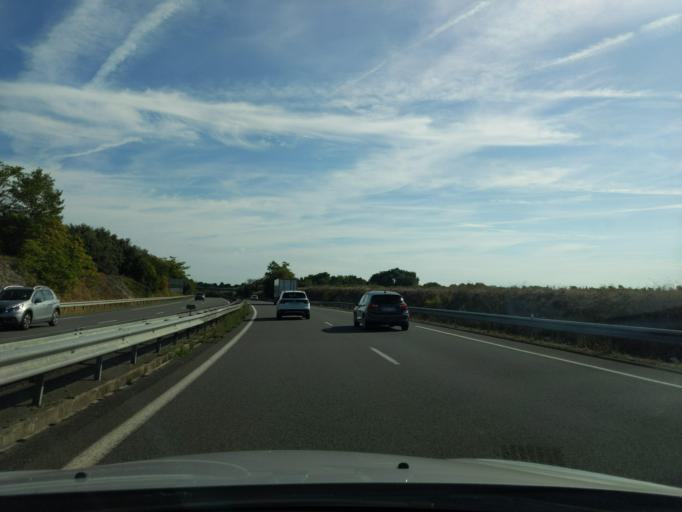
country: FR
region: Poitou-Charentes
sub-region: Departement de la Charente
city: Gensac-la-Pallue
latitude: 45.6639
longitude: -0.2195
